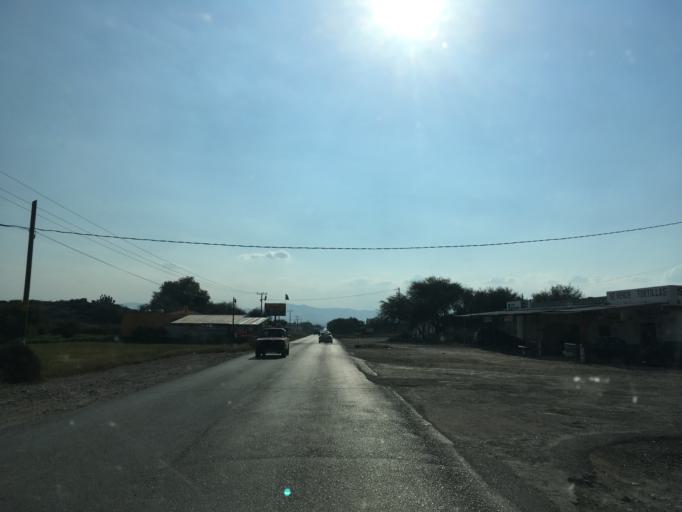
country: MX
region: Hidalgo
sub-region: Ixmiquilpan
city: El Nith
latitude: 20.5548
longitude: -99.1603
